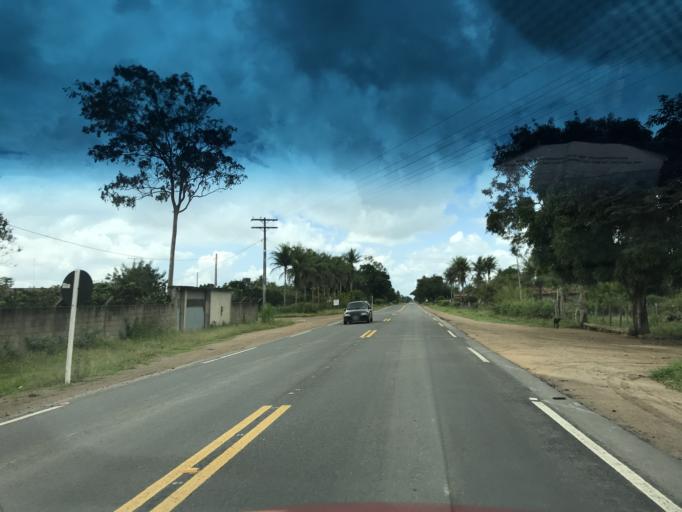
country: BR
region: Bahia
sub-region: Conceicao Do Almeida
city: Conceicao do Almeida
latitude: -12.7179
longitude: -39.2178
